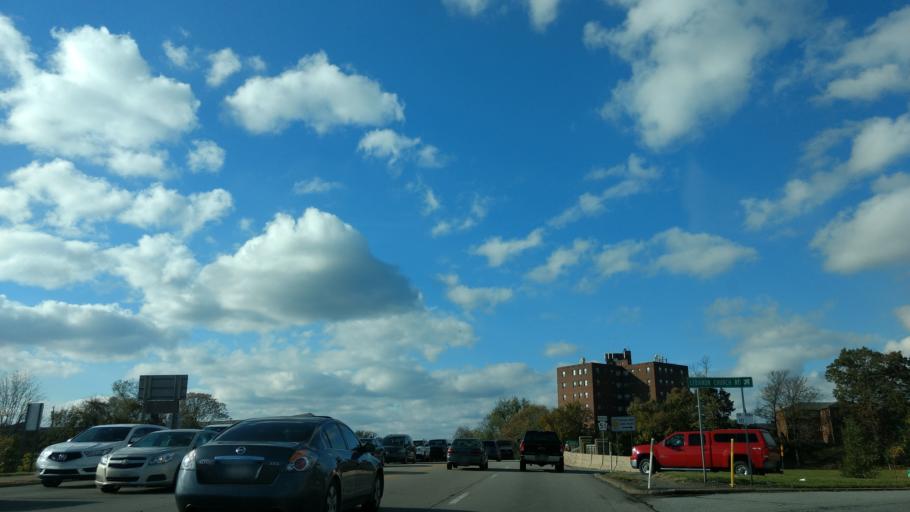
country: US
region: Pennsylvania
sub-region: Allegheny County
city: Pleasant Hills
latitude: 40.3411
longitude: -79.9650
